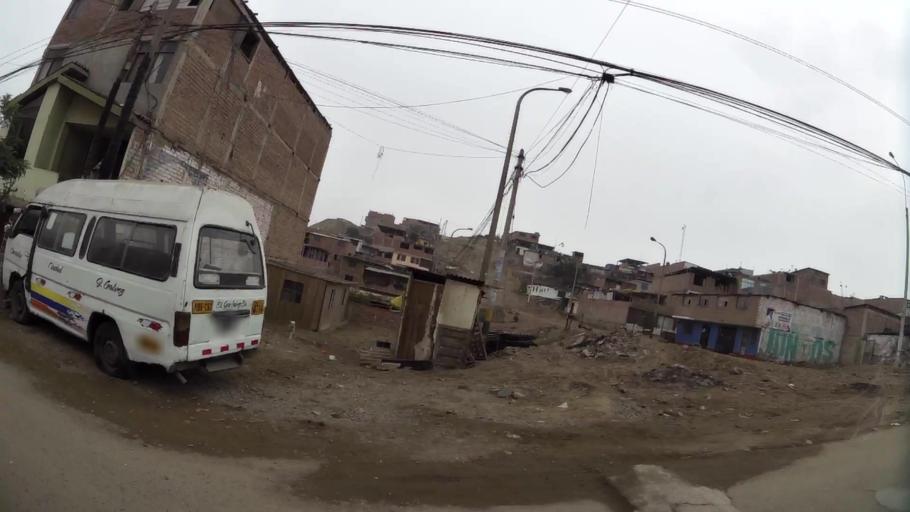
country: PE
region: Lima
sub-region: Lima
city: Surco
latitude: -12.2208
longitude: -76.9182
